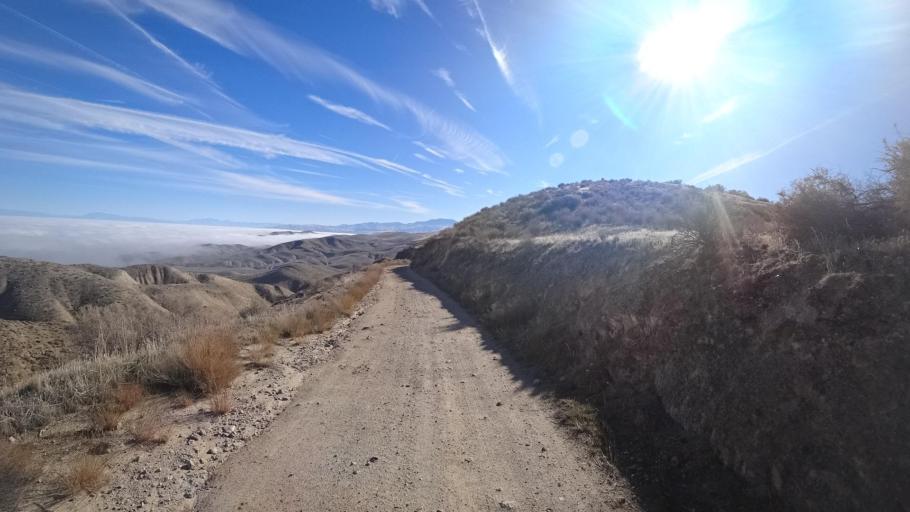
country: US
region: California
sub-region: Kern County
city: Maricopa
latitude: 35.0146
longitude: -119.4705
